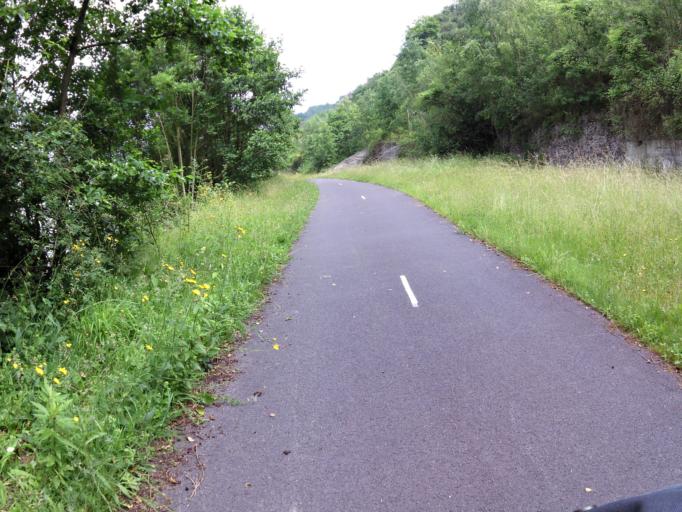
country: FR
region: Champagne-Ardenne
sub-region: Departement des Ardennes
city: Vireux-Wallerand
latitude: 50.0989
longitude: 4.7661
